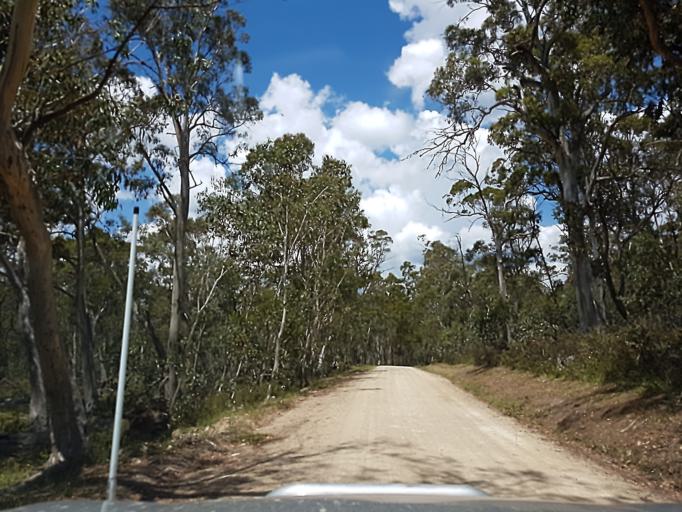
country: AU
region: New South Wales
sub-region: Snowy River
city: Jindabyne
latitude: -36.8786
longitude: 148.0840
